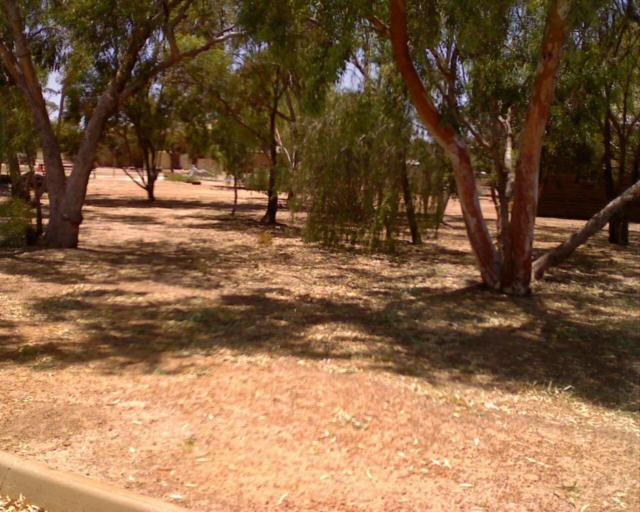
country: AU
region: Western Australia
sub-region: Wongan-Ballidu
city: Wongan Hills
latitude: -30.8275
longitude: 117.4808
